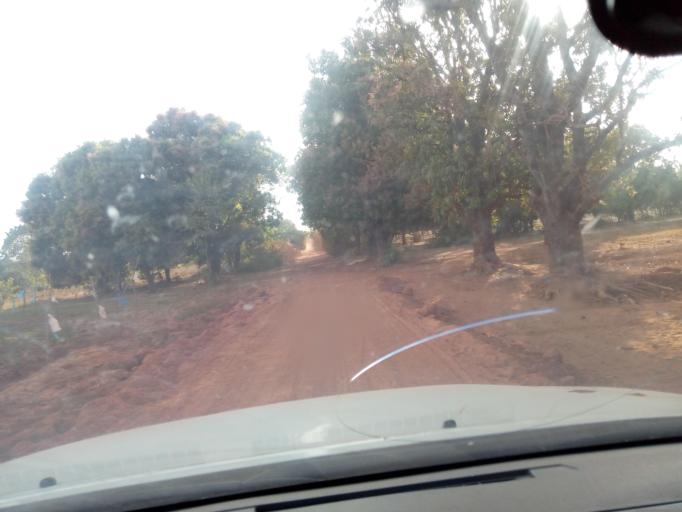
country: ML
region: Sikasso
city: Sikasso
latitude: 11.4186
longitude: -5.5654
